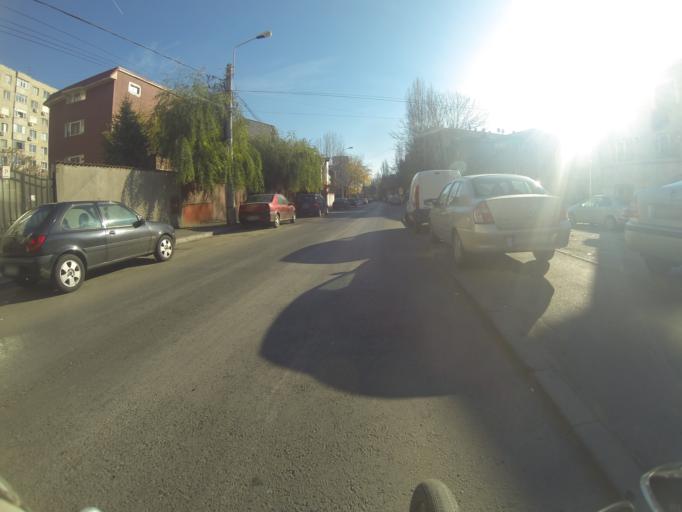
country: RO
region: Bucuresti
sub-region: Municipiul Bucuresti
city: Bucuresti
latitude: 44.4046
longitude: 26.0651
